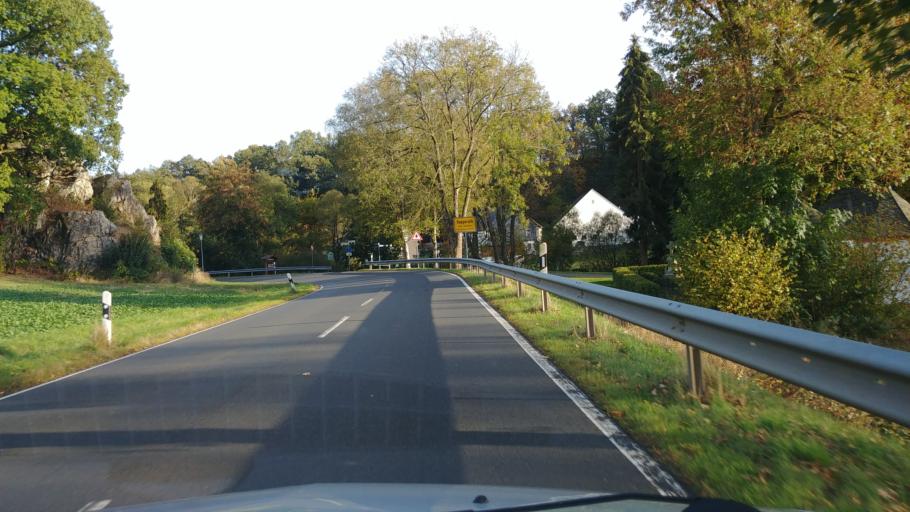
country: DE
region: Rheinland-Pfalz
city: Morbach
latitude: 49.8176
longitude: 7.0931
